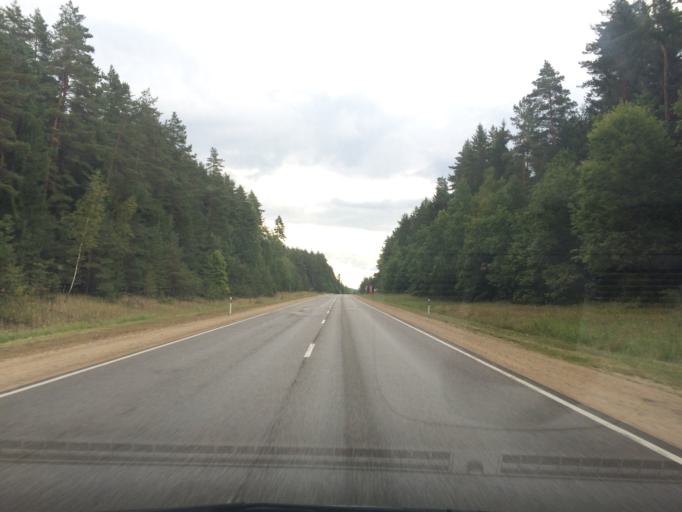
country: LV
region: Plavinu
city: Plavinas
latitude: 56.5884
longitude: 25.5821
